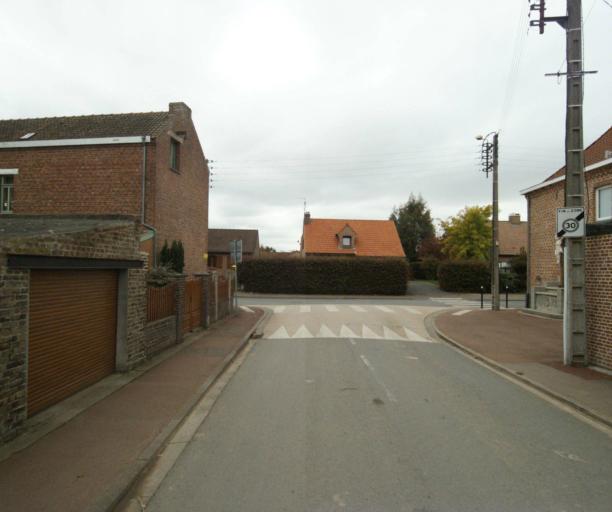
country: FR
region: Nord-Pas-de-Calais
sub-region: Departement du Nord
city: Marquillies
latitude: 50.5512
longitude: 2.8690
